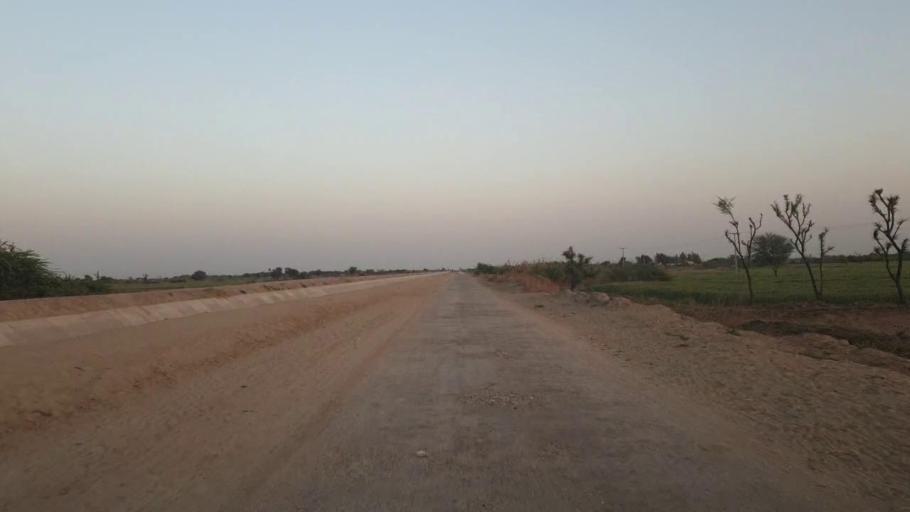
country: PK
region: Sindh
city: Dhoro Naro
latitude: 25.4466
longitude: 69.6281
